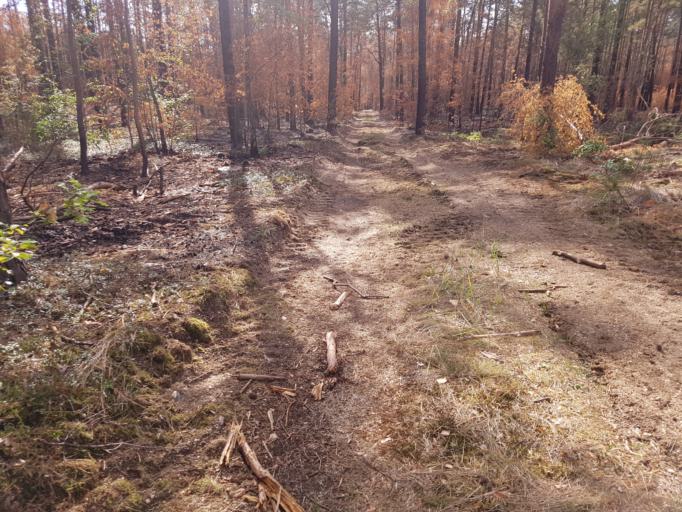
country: DE
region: Brandenburg
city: Finsterwalde
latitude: 51.6304
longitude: 13.6724
